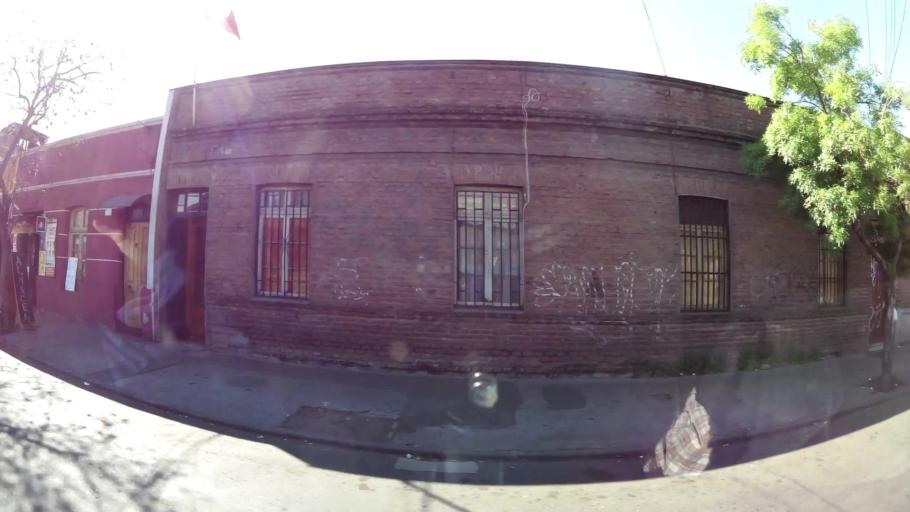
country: CL
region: Santiago Metropolitan
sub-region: Provincia de Santiago
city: Santiago
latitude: -33.4081
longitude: -70.6427
